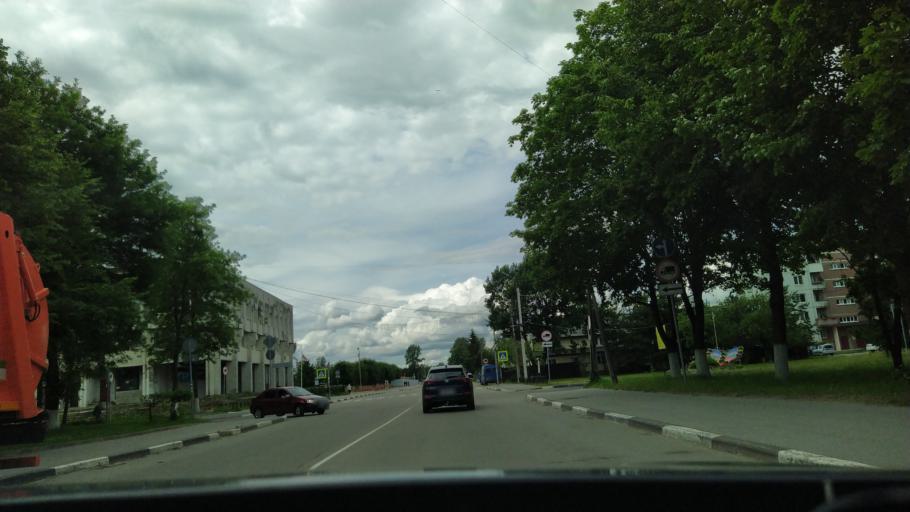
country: RU
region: Leningrad
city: Kirovsk
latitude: 59.8813
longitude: 30.9890
